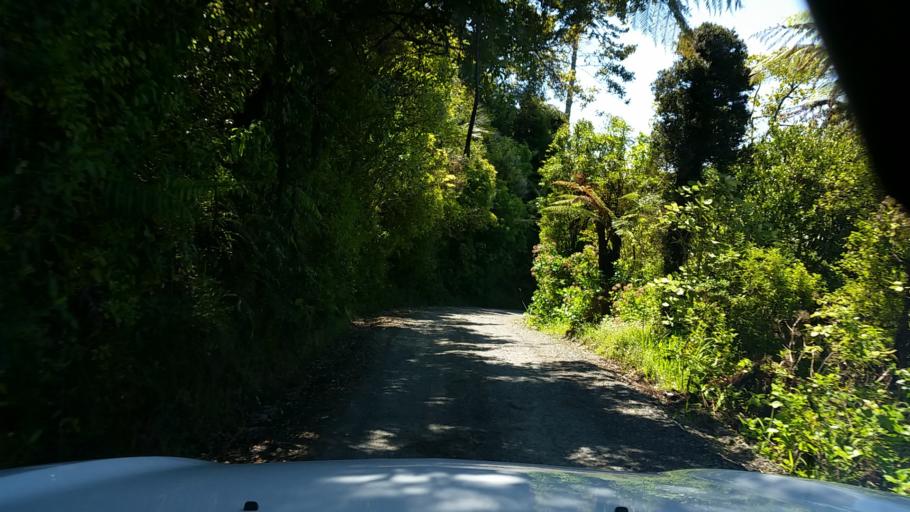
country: NZ
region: Auckland
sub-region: Auckland
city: Titirangi
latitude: -36.9290
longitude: 174.5814
